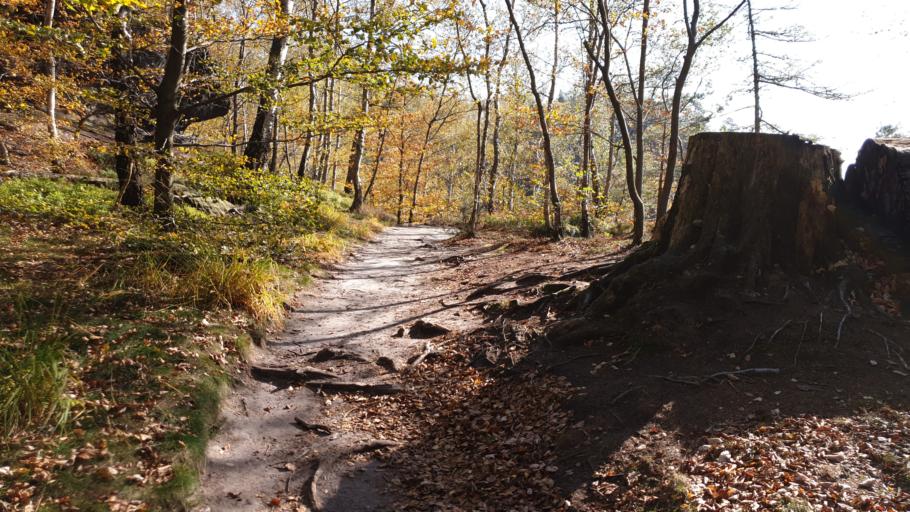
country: DE
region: Saxony
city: Bad Schandau
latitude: 50.9070
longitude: 14.2337
